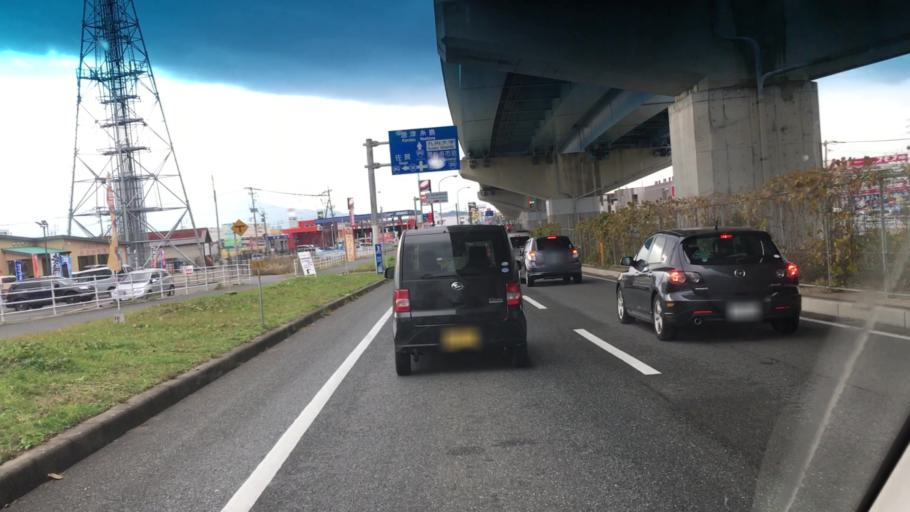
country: JP
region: Fukuoka
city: Maebaru-chuo
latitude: 33.5664
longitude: 130.2446
